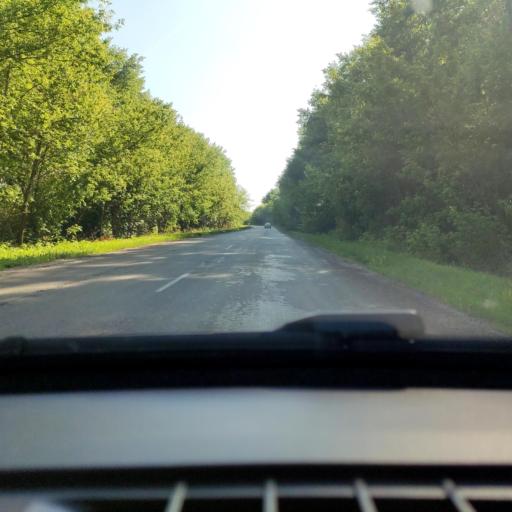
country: RU
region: Voronezj
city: Panino
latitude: 51.6190
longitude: 40.0199
